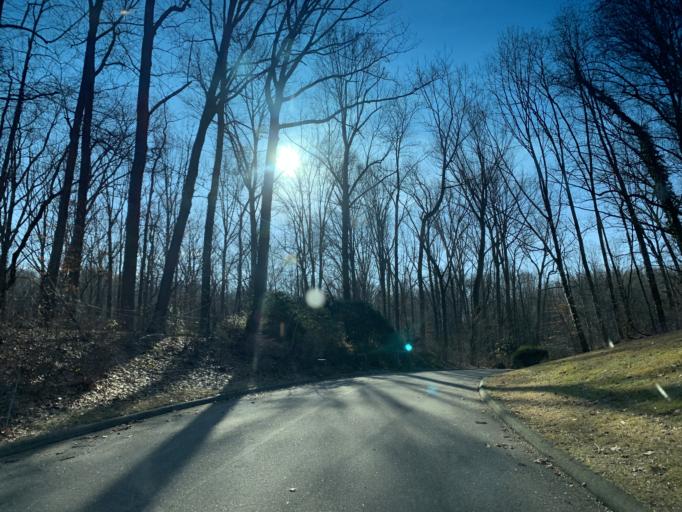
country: US
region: Maryland
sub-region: Harford County
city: Riverside
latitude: 39.5770
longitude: -76.2434
